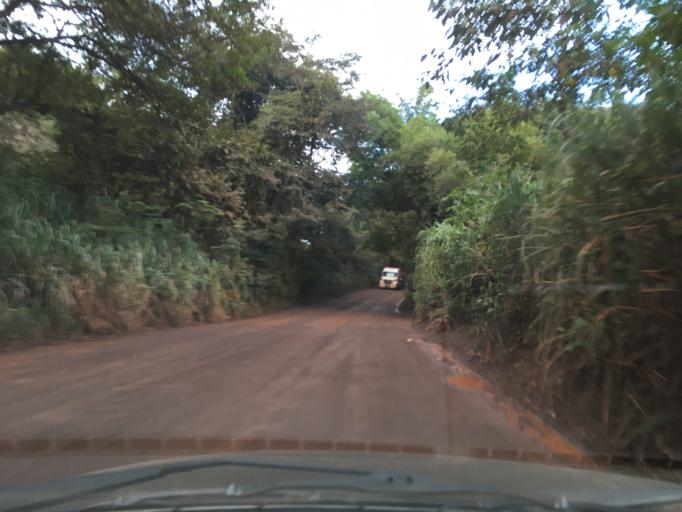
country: BR
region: Minas Gerais
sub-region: Brumadinho
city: Brumadinho
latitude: -20.1053
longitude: -44.2099
